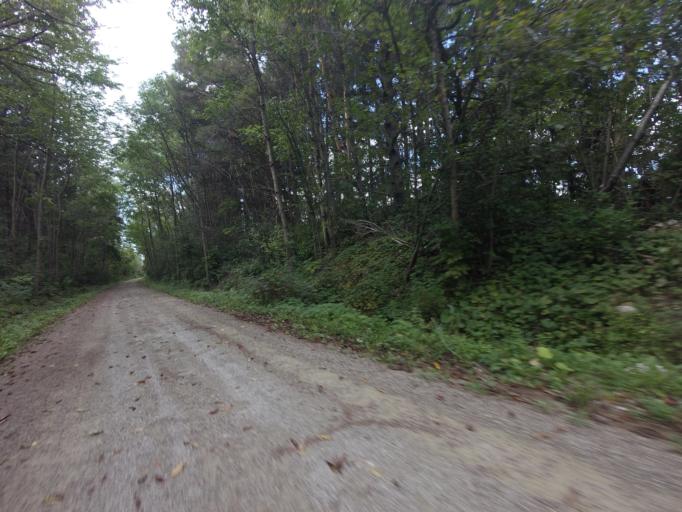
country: CA
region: Ontario
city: Huron East
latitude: 43.7246
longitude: -81.4074
